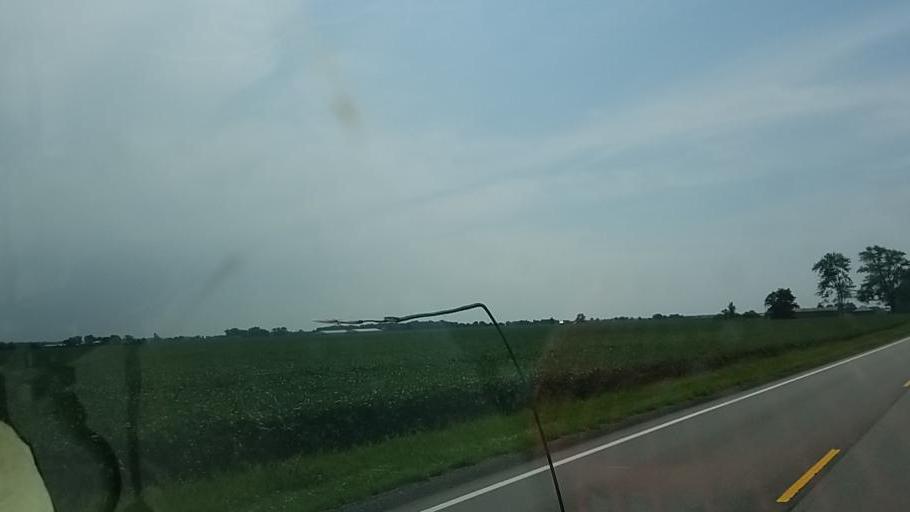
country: US
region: Ohio
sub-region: Marion County
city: Marion
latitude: 40.6106
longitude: -83.0315
